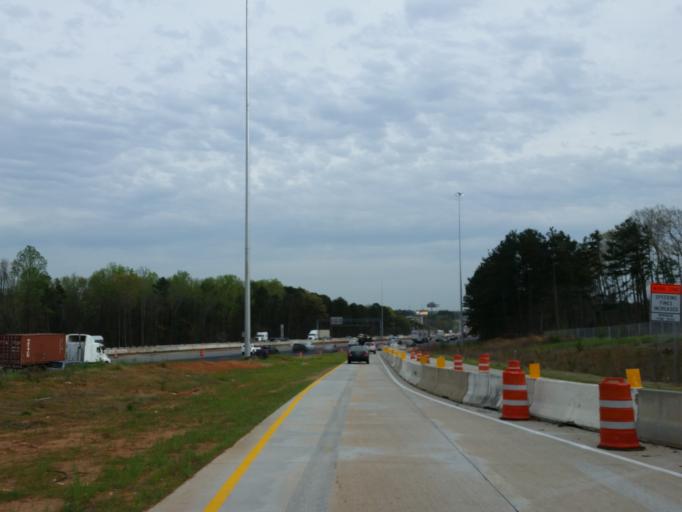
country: US
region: Georgia
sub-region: Henry County
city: Stockbridge
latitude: 33.4800
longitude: -84.2174
